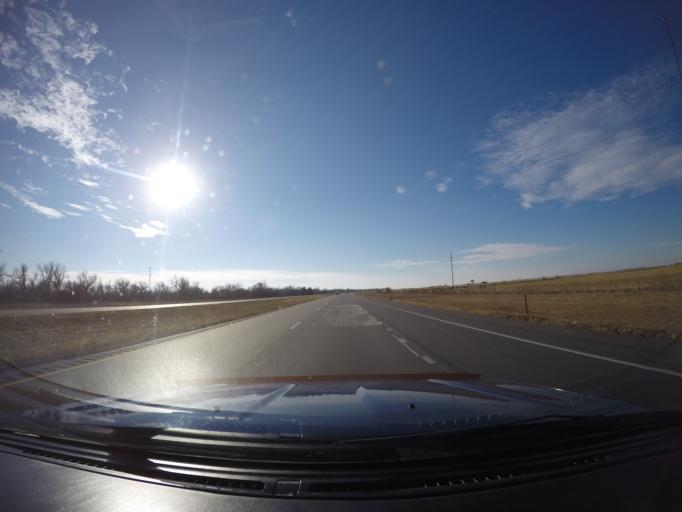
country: US
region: Nebraska
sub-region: Buffalo County
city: Kearney
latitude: 40.6854
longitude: -98.9561
